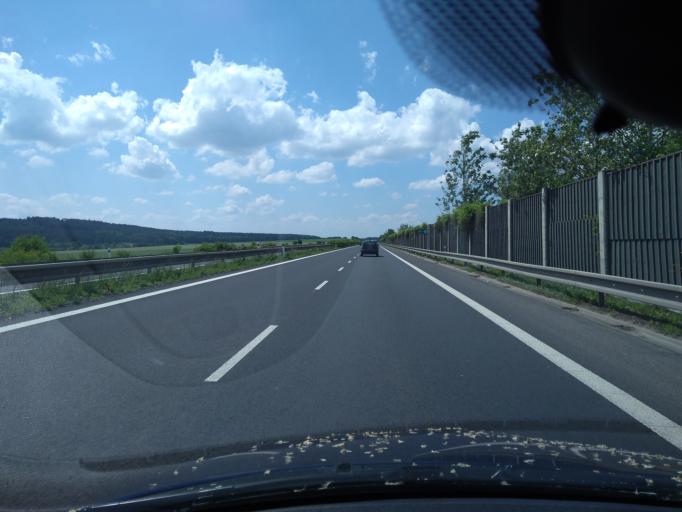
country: CZ
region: Plzensky
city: Stenovice
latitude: 49.6742
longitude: 13.3571
